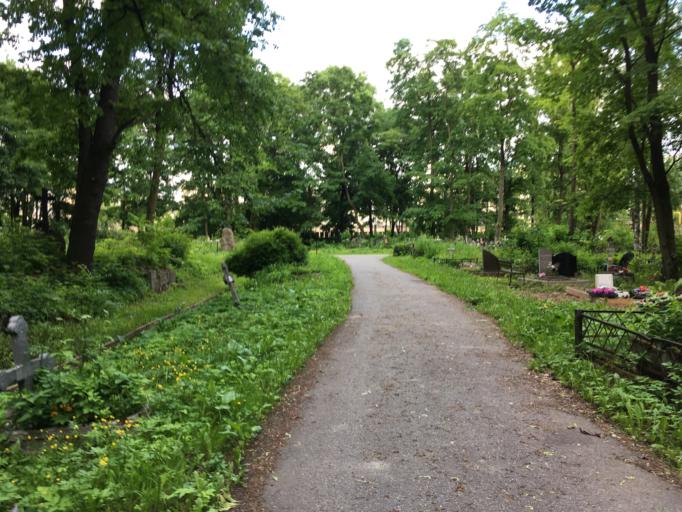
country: RU
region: St.-Petersburg
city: Centralniy
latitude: 59.9019
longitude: 30.3721
